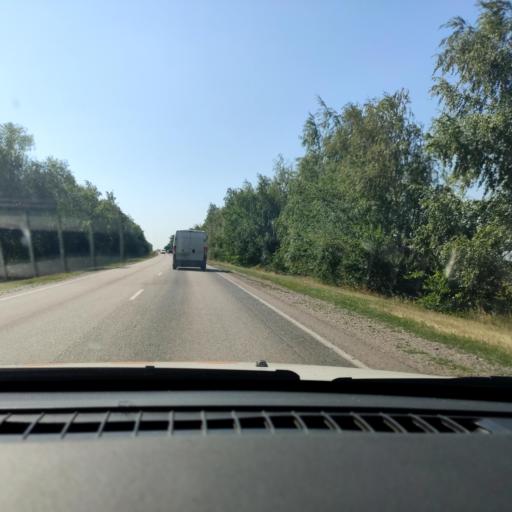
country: RU
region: Voronezj
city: Liski
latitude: 50.8015
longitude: 39.3344
